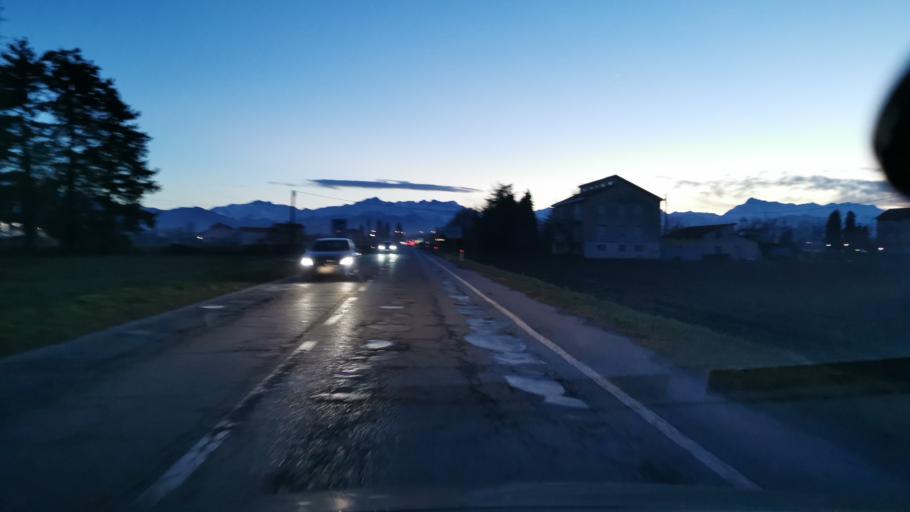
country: IT
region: Piedmont
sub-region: Provincia di Cuneo
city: Roata Rossi
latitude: 44.4372
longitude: 7.5619
